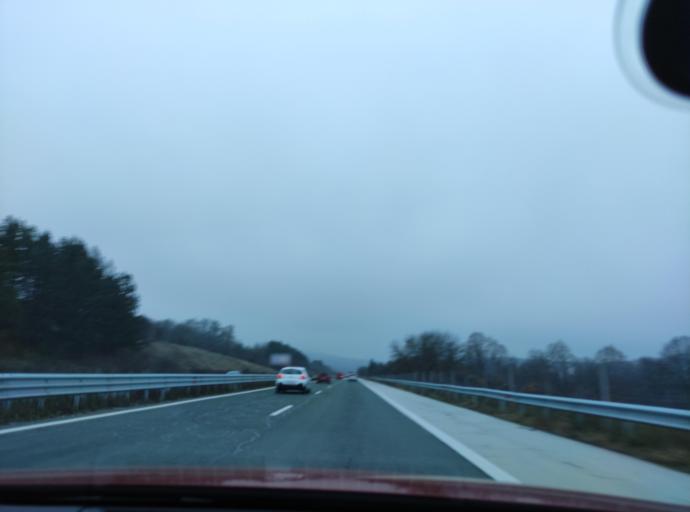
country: BG
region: Lovech
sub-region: Obshtina Yablanitsa
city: Yablanitsa
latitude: 42.9992
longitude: 24.0801
